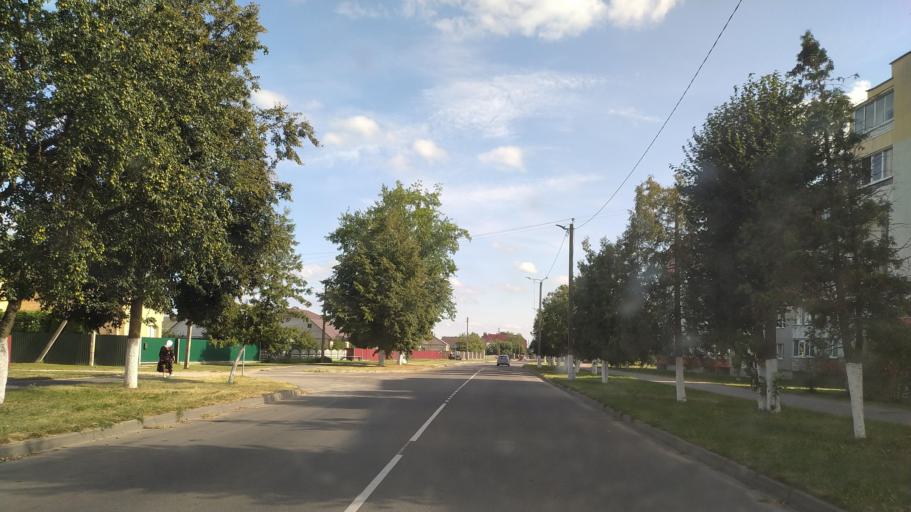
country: BY
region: Brest
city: Byaroza
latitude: 52.5316
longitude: 24.9857
